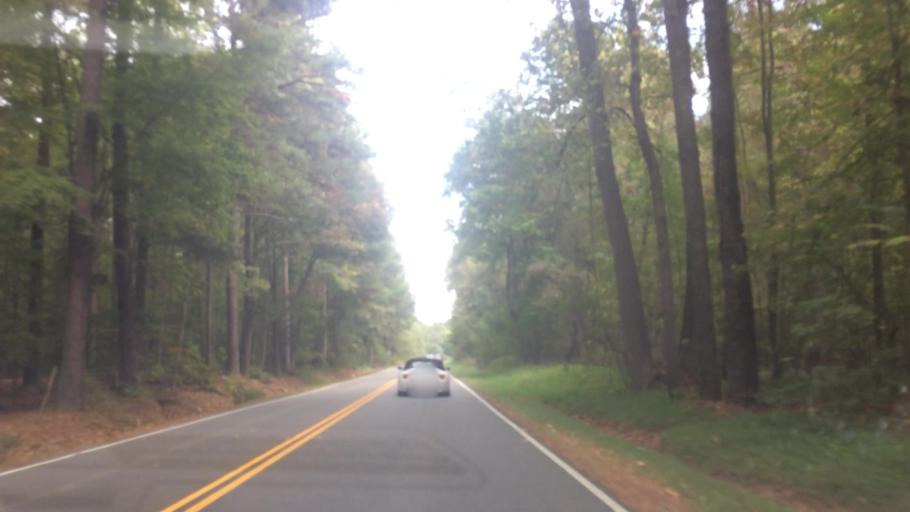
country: US
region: Virginia
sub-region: City of Williamsburg
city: Williamsburg
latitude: 37.3140
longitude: -76.7205
